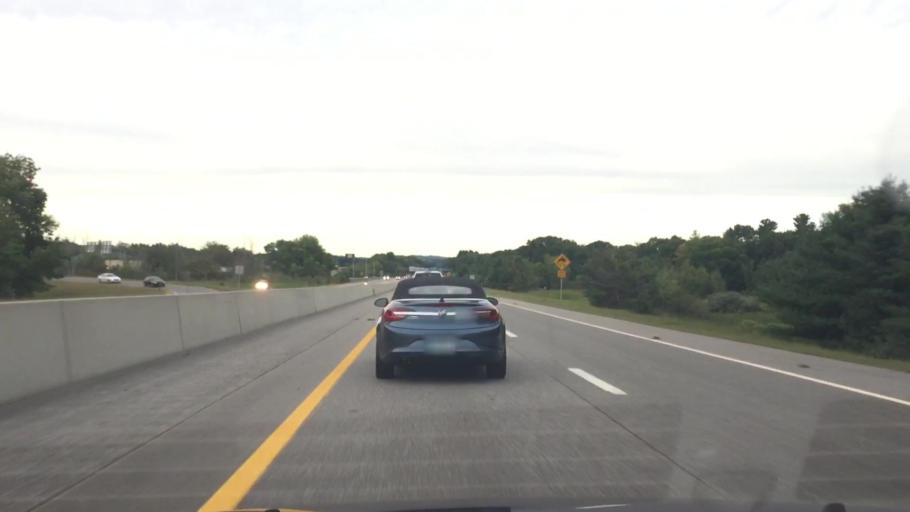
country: US
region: New Hampshire
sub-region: Hillsborough County
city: Bedford
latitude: 42.9498
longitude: -71.4724
